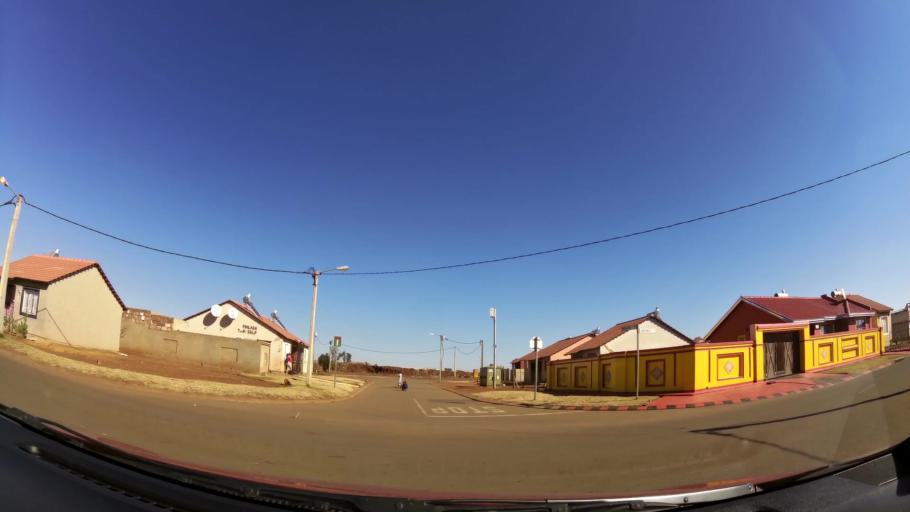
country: ZA
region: Gauteng
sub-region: City of Johannesburg Metropolitan Municipality
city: Soweto
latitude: -26.2413
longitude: 27.7983
